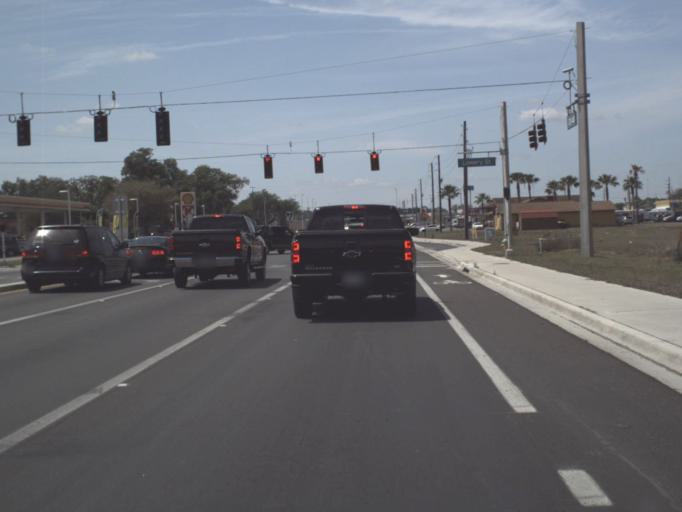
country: US
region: Florida
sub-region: Sumter County
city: Bushnell
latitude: 28.6687
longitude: -82.1368
